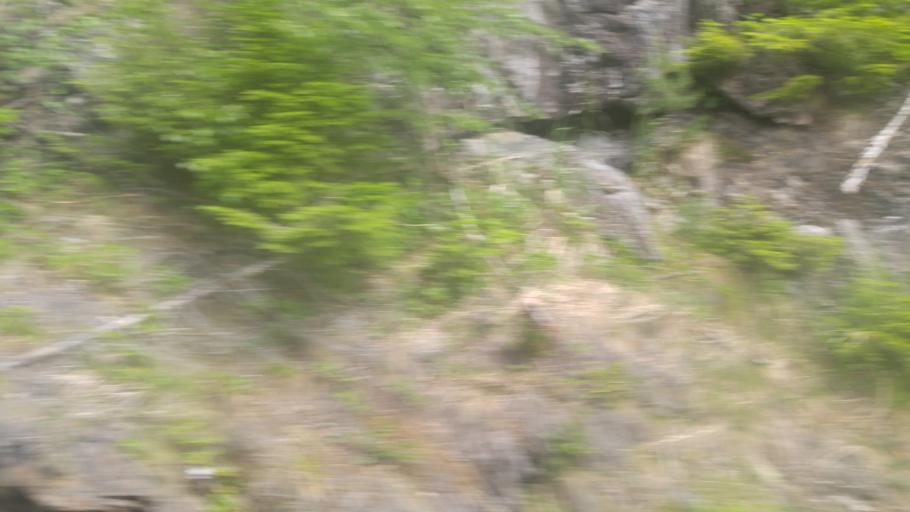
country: NO
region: Sor-Trondelag
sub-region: Selbu
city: Mebonden
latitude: 62.9664
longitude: 10.9593
